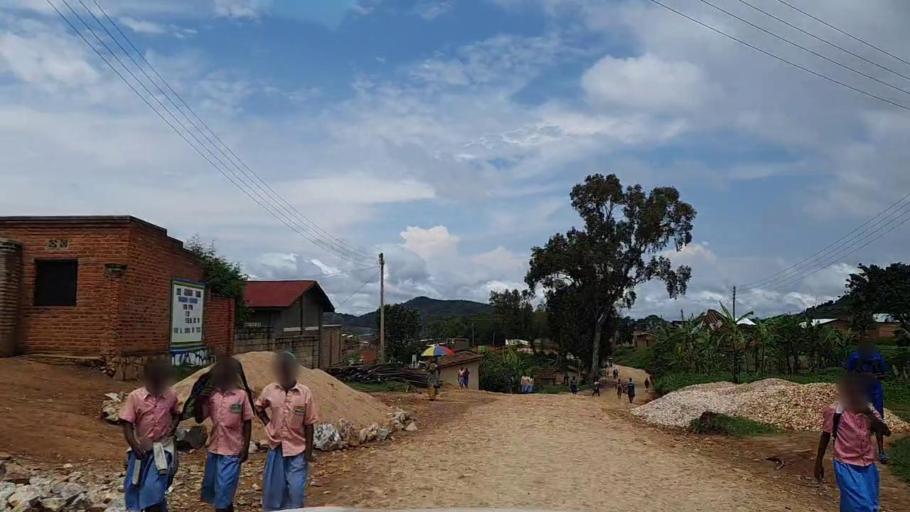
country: RW
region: Southern Province
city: Gikongoro
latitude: -2.3308
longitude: 29.5292
